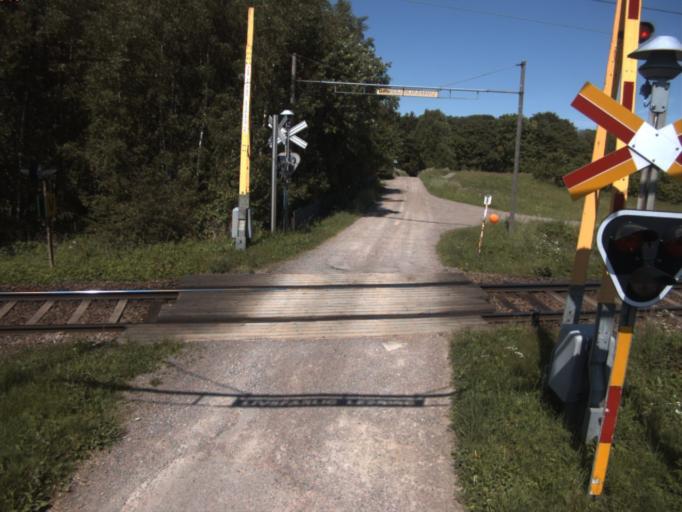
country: SE
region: Skane
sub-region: Helsingborg
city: Gantofta
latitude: 55.9974
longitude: 12.7840
